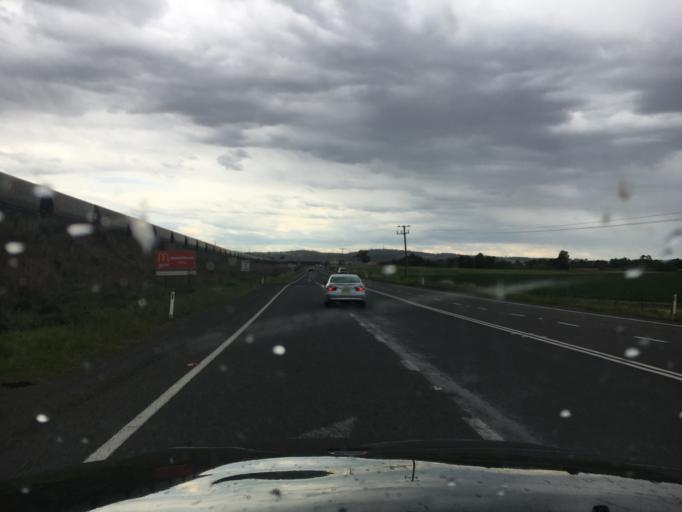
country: AU
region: New South Wales
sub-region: Muswellbrook
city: Muswellbrook
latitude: -32.2104
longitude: 150.8957
